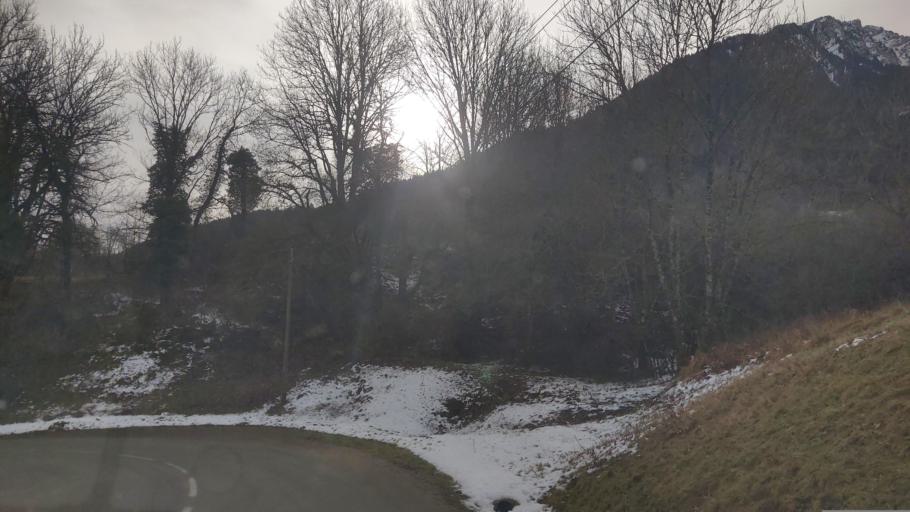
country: FR
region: Rhone-Alpes
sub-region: Departement de la Haute-Savoie
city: Doussard
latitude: 45.6791
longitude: 6.1315
